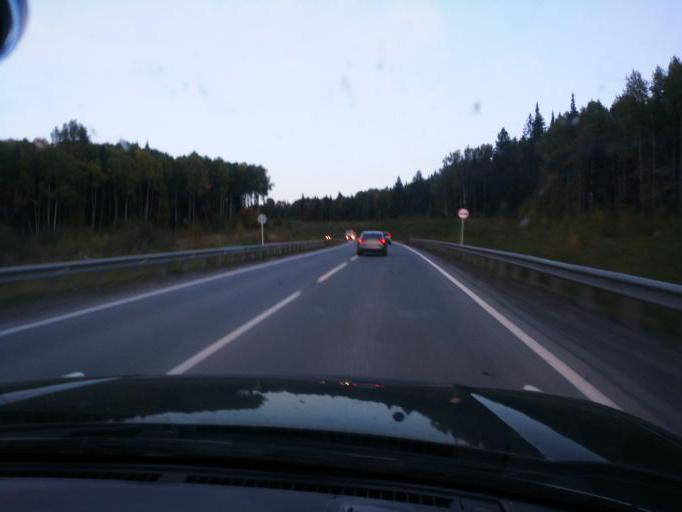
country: RU
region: Perm
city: Sylva
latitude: 58.2971
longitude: 56.8009
